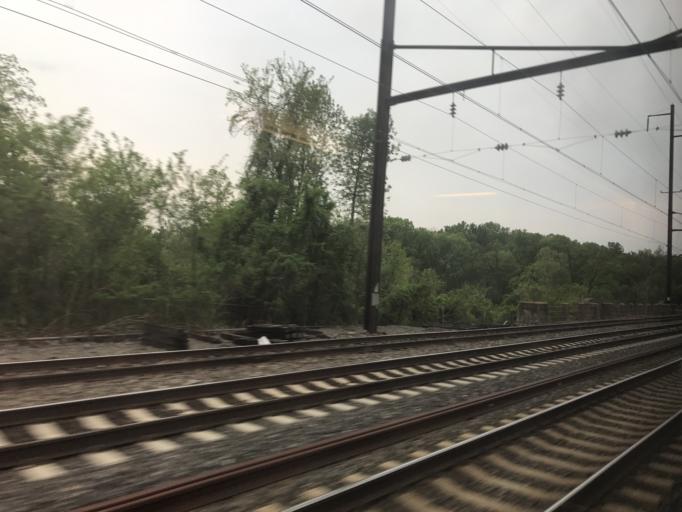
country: US
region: Maryland
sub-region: Baltimore County
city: Lansdowne
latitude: 39.2879
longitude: -76.6630
